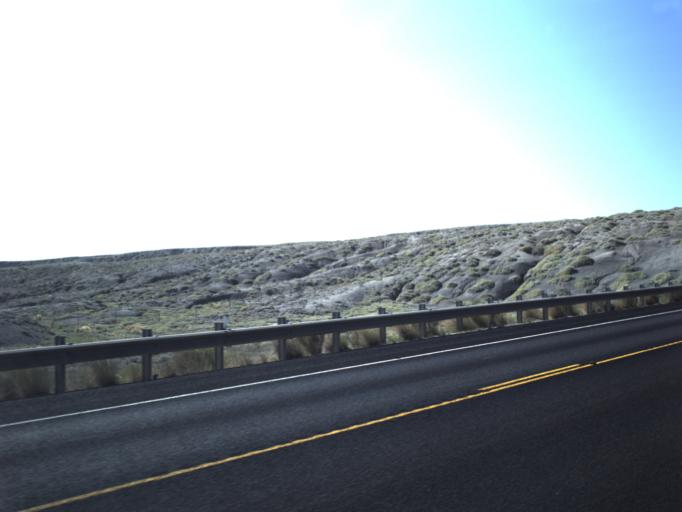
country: US
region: Utah
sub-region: Emery County
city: Ferron
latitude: 39.0421
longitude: -111.1254
